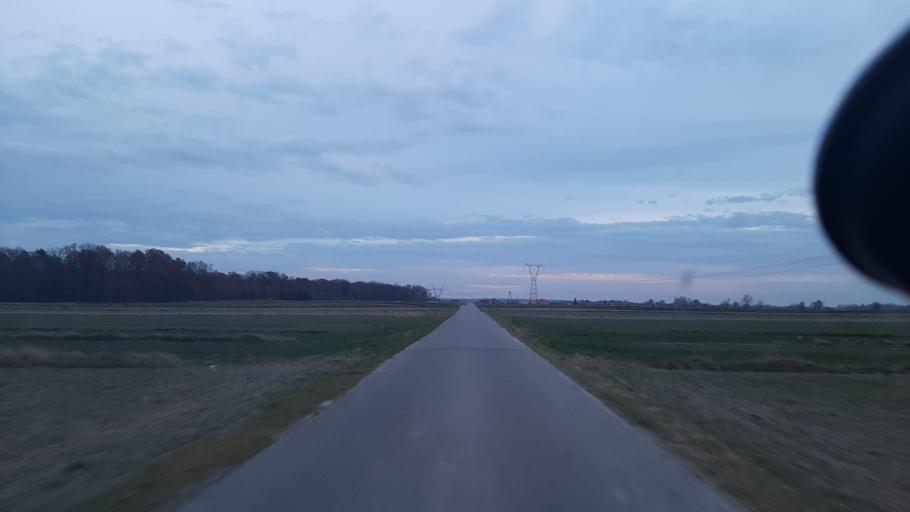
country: PL
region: Lublin Voivodeship
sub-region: Powiat lubelski
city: Garbow
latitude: 51.3742
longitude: 22.3752
